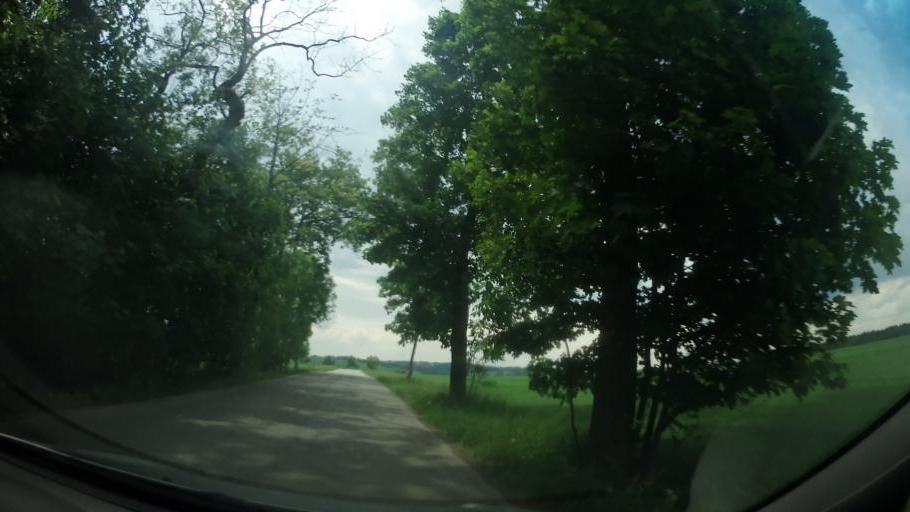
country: CZ
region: South Moravian
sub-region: Okres Brno-Venkov
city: Lomnice
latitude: 49.4781
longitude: 16.4376
